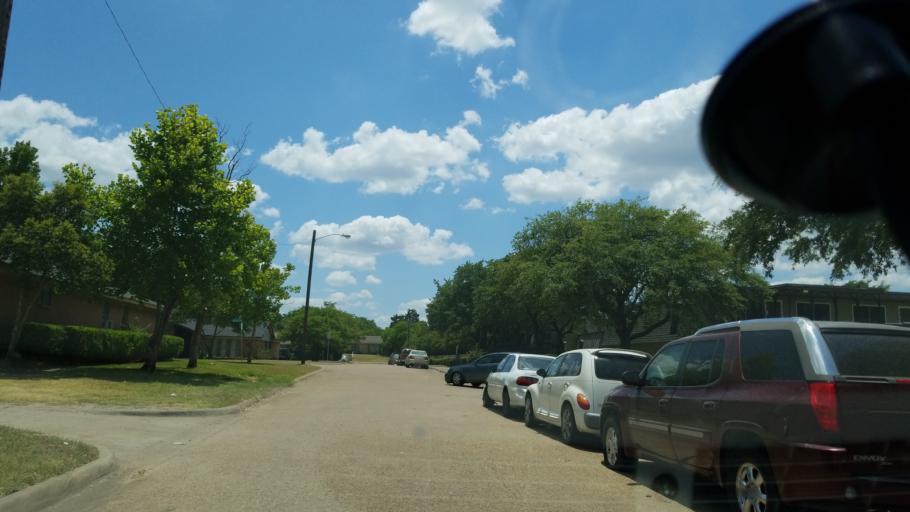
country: US
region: Texas
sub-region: Dallas County
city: Cockrell Hill
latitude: 32.6932
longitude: -96.8537
